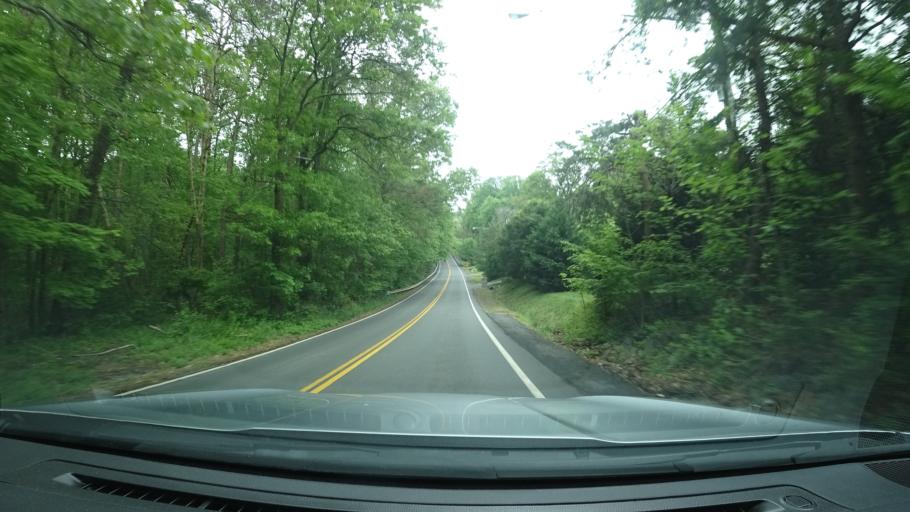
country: US
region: Virginia
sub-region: Fairfax County
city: Oak Hill
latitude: 38.9095
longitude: -77.3615
